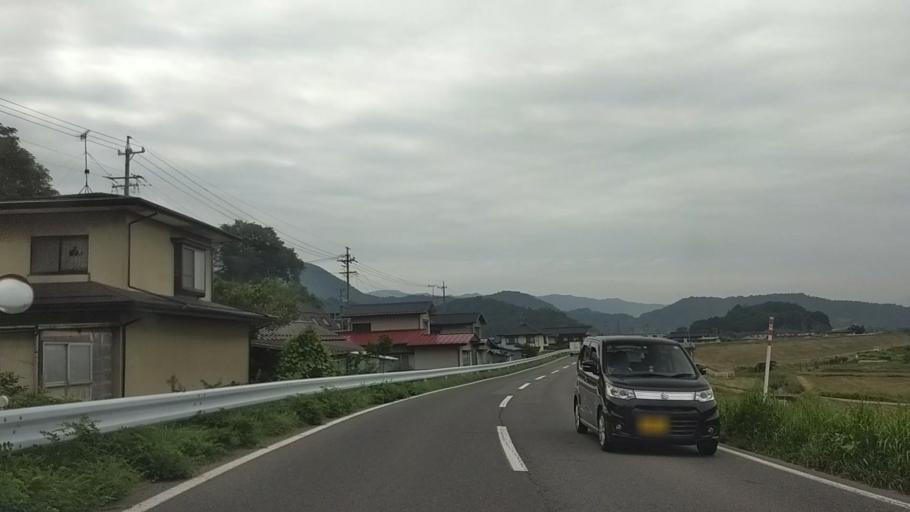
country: JP
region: Nagano
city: Nagano-shi
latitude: 36.6039
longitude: 138.2256
